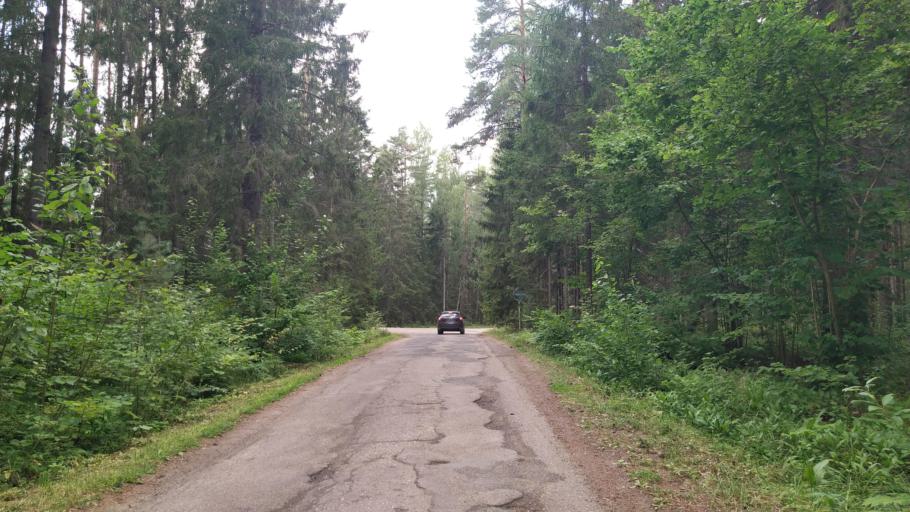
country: RU
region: Pskov
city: Pushkinskiye Gory
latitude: 57.0581
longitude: 28.9413
